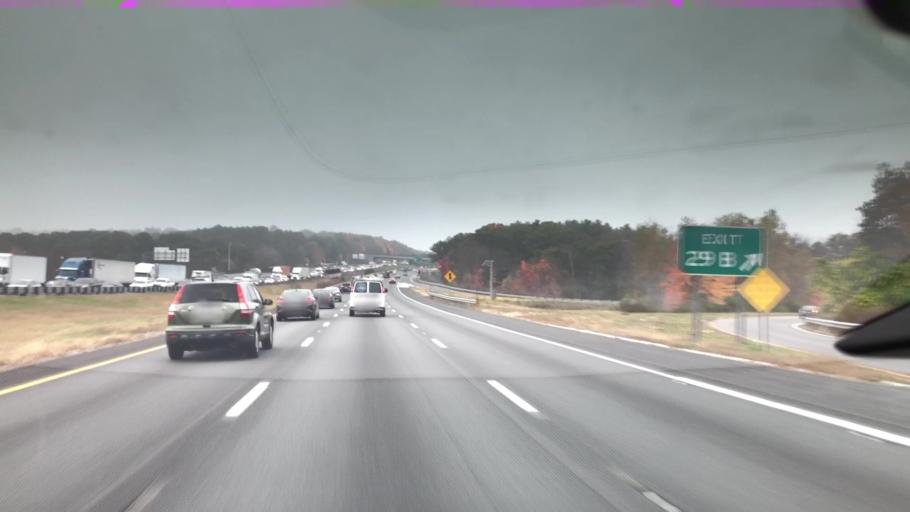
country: US
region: Massachusetts
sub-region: Middlesex County
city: Littleton Common
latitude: 42.5233
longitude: -71.5063
